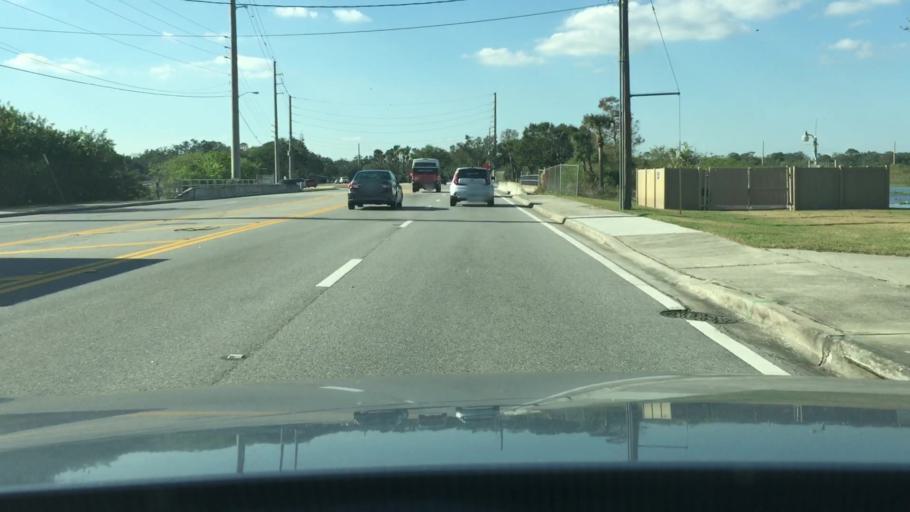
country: US
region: Florida
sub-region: Osceola County
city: Kissimmee
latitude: 28.2928
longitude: -81.3946
